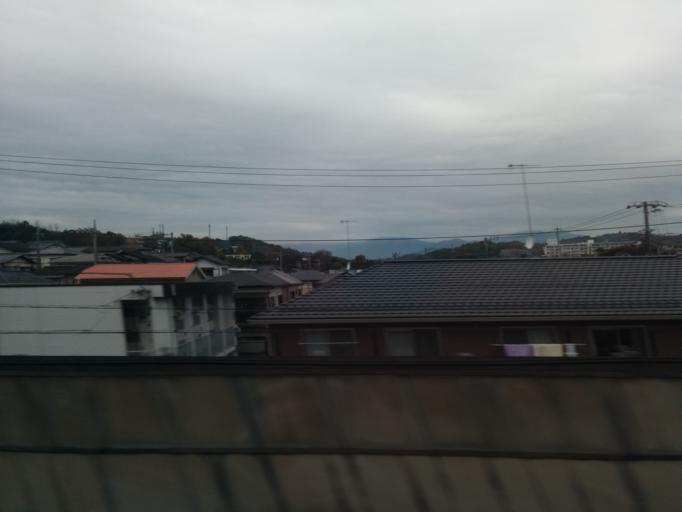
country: JP
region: Kanagawa
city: Ninomiya
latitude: 35.3069
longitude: 139.2470
